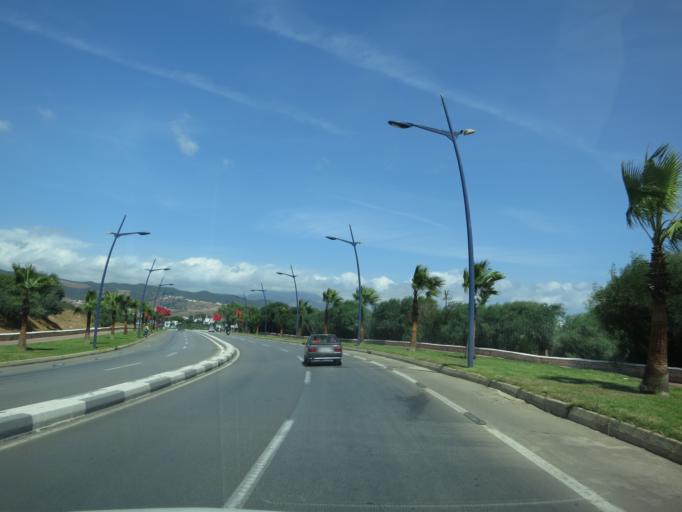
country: ES
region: Ceuta
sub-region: Ceuta
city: Ceuta
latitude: 35.7850
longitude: -5.3514
